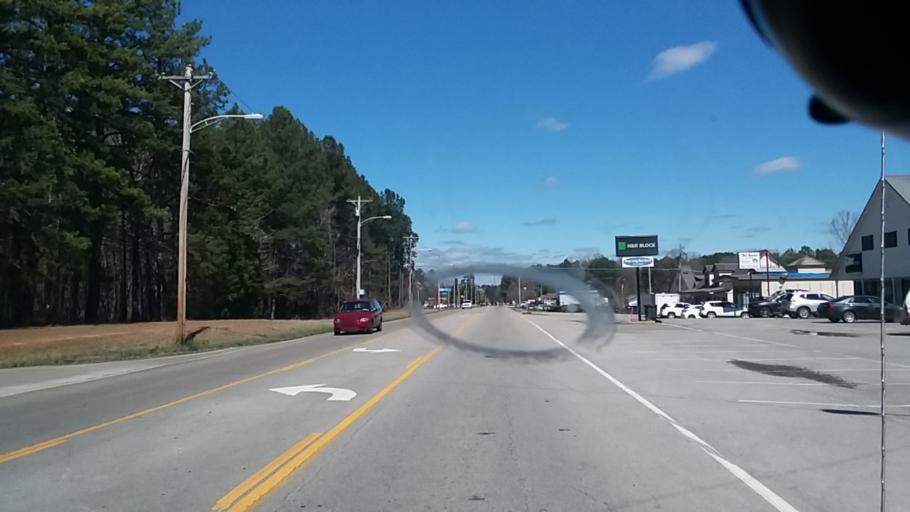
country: US
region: Mississippi
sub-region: Tishomingo County
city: Iuka
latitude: 34.8014
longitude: -88.2043
